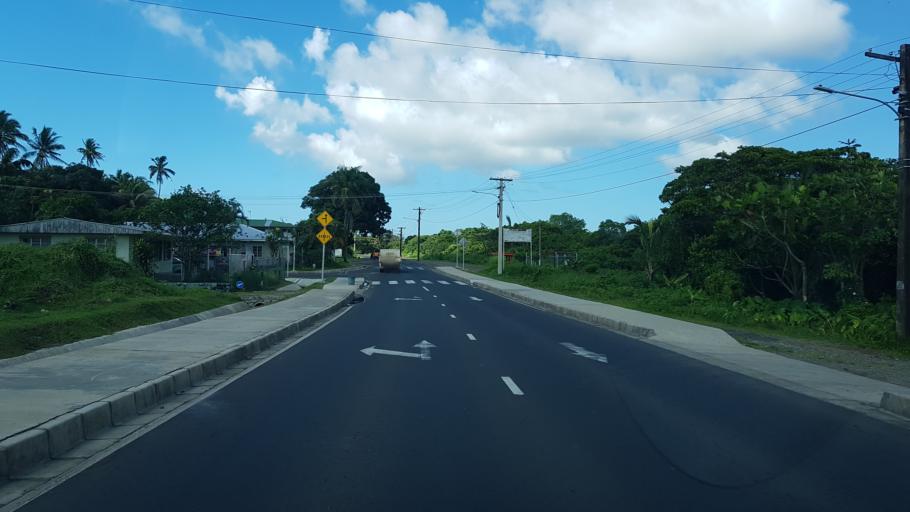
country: FJ
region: Central
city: Suva
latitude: -18.1392
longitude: 178.4578
